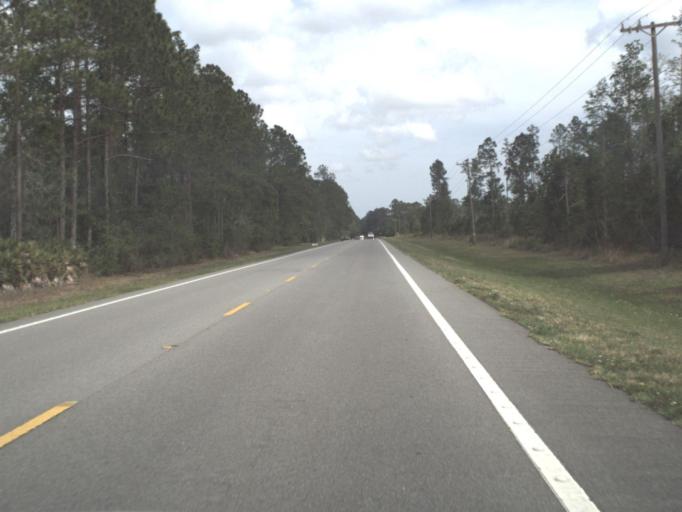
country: US
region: Florida
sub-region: Flagler County
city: Bunnell
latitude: 29.4727
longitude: -81.3247
